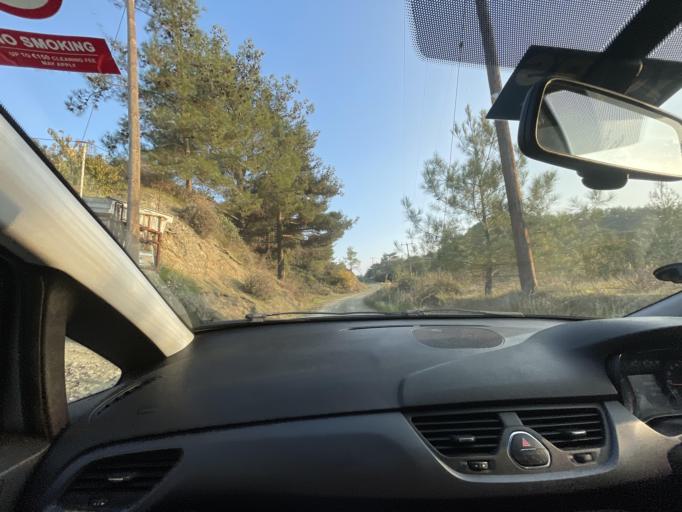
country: CY
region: Limassol
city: Pelendri
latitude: 34.8870
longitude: 32.9732
